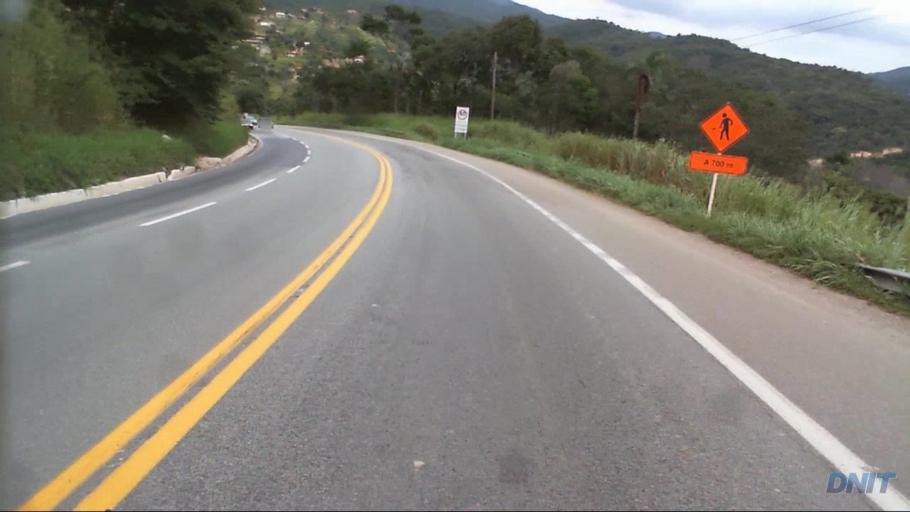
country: BR
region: Minas Gerais
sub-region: Caete
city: Caete
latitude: -19.7816
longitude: -43.6610
